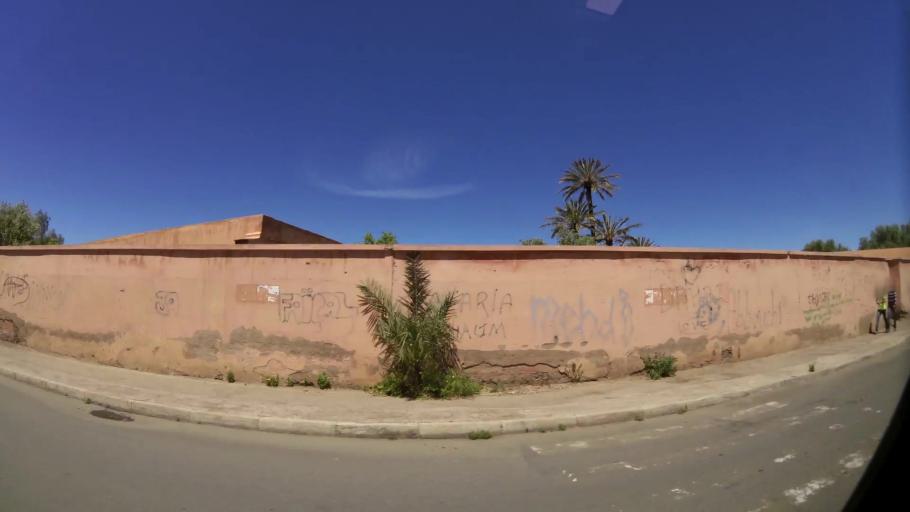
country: MA
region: Marrakech-Tensift-Al Haouz
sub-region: Marrakech
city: Marrakesh
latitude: 31.6492
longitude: -7.9903
